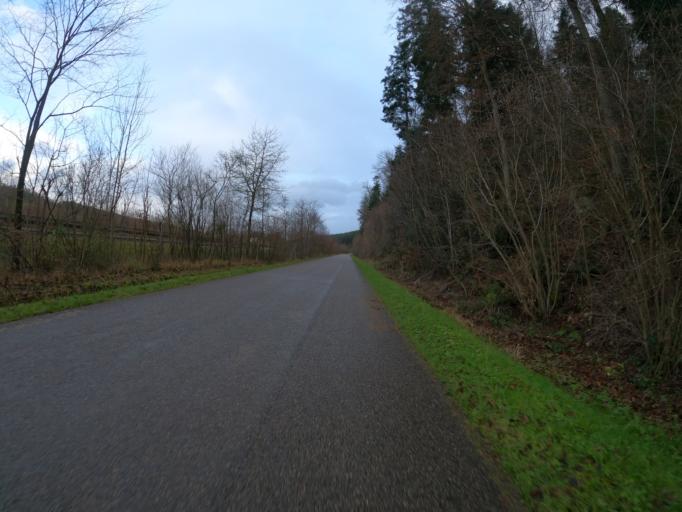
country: DE
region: Baden-Wuerttemberg
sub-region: Regierungsbezirk Stuttgart
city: Lorch
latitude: 48.7911
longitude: 9.7195
